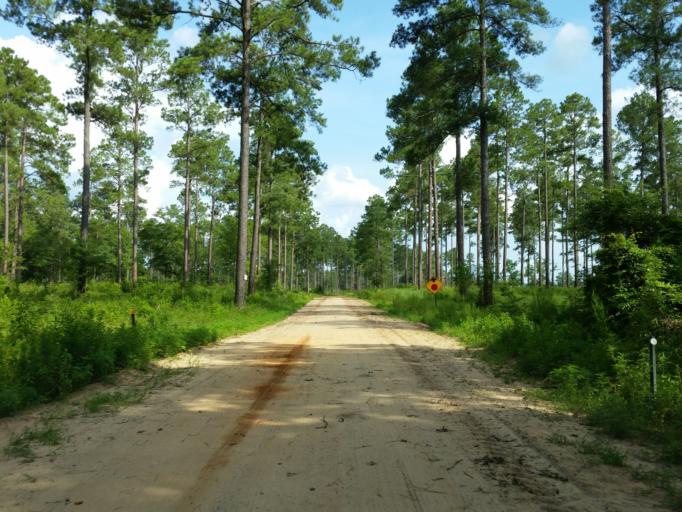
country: US
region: Georgia
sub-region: Lee County
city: Leesburg
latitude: 31.7632
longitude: -84.0197
